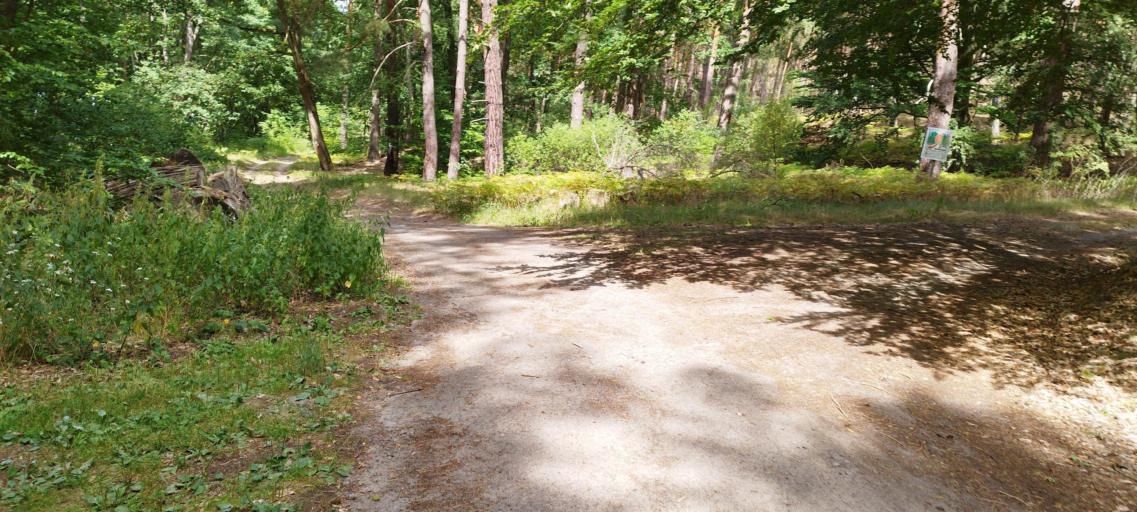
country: DE
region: Brandenburg
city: Mixdorf
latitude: 52.1481
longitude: 14.4601
